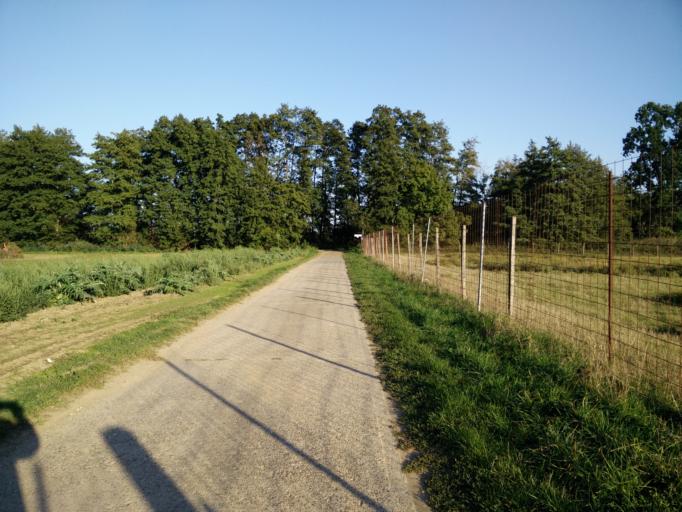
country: DE
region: Rheinland-Pfalz
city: Hergersweiler
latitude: 49.1005
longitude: 8.0917
